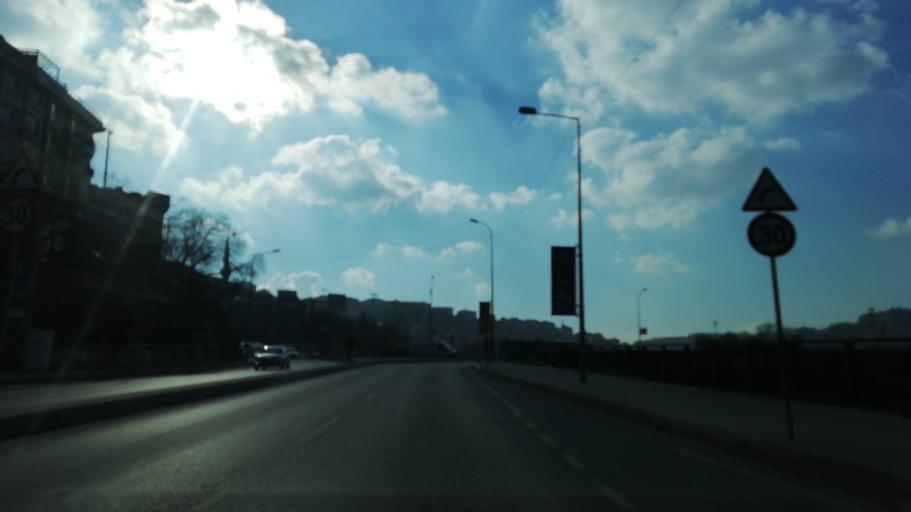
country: TR
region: Istanbul
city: Sisli
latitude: 41.0766
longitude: 28.9500
